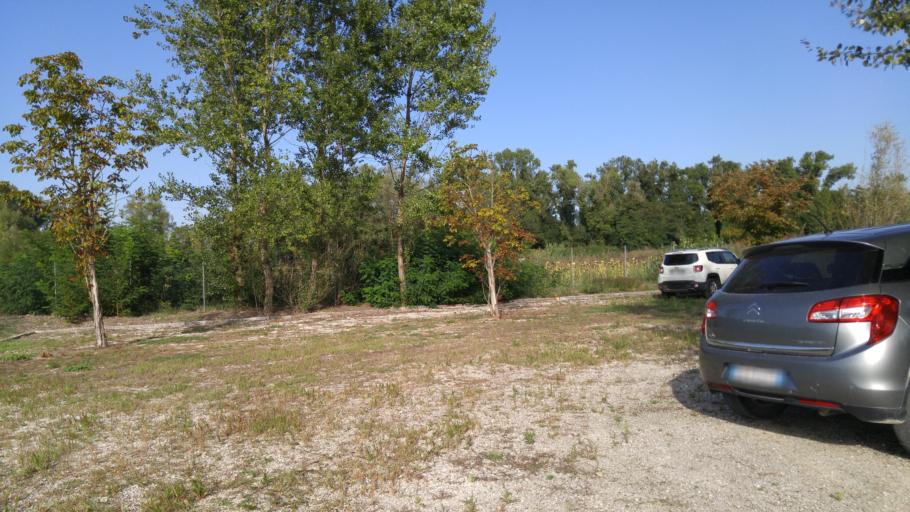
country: IT
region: The Marches
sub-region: Provincia di Pesaro e Urbino
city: Sant'Ippolito
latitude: 43.7000
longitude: 12.8497
